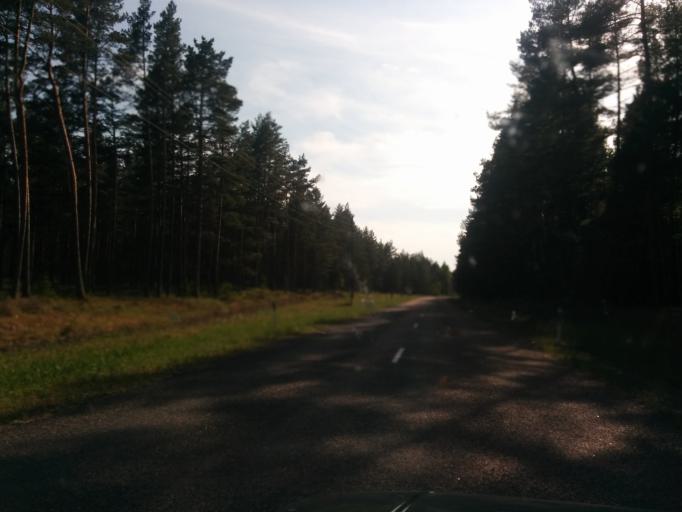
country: LV
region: Dundaga
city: Dundaga
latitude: 57.6616
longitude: 22.2936
